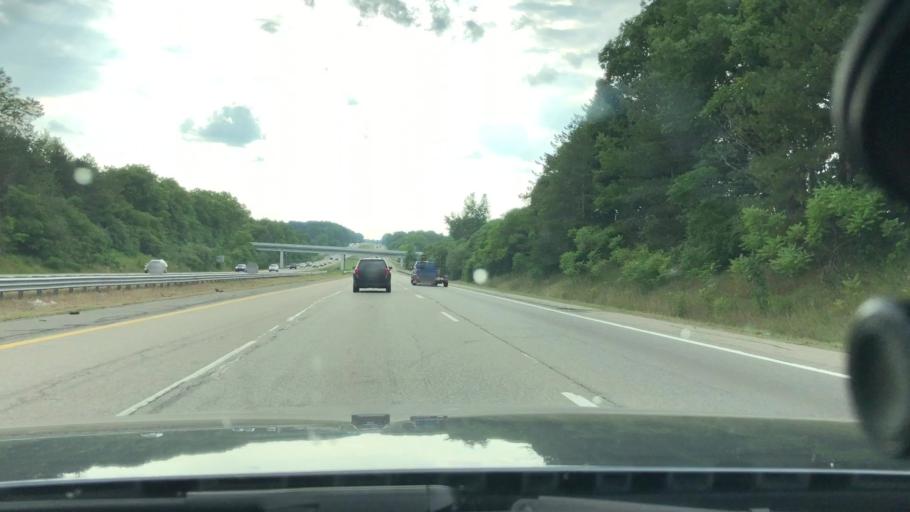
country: US
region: Michigan
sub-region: Washtenaw County
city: Dexter
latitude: 42.2982
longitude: -83.8942
